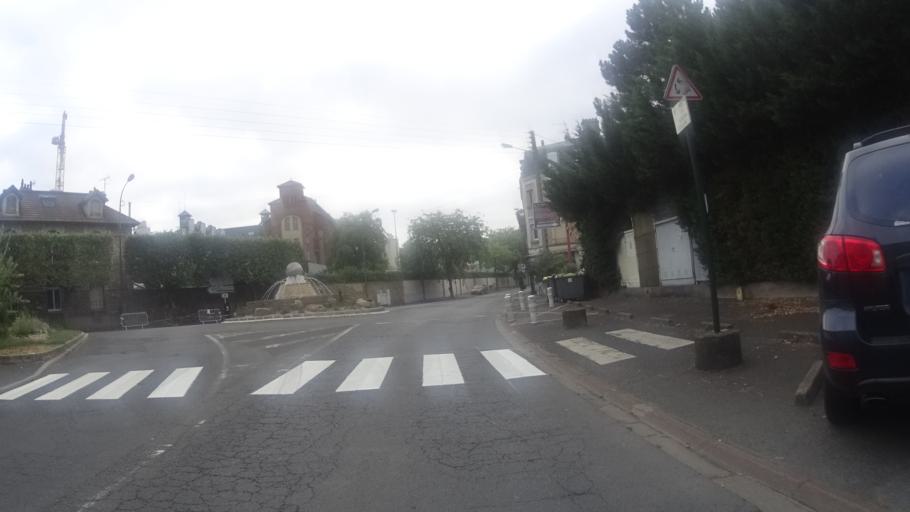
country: FR
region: Ile-de-France
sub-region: Departement de l'Essonne
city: Corbeil-Essonnes
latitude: 48.6137
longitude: 2.4769
